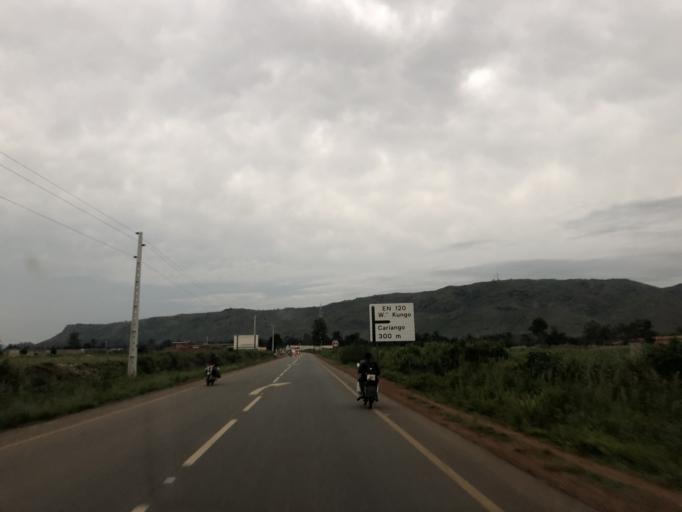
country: AO
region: Cuanza Sul
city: Uacu Cungo
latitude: -11.3443
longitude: 15.1041
